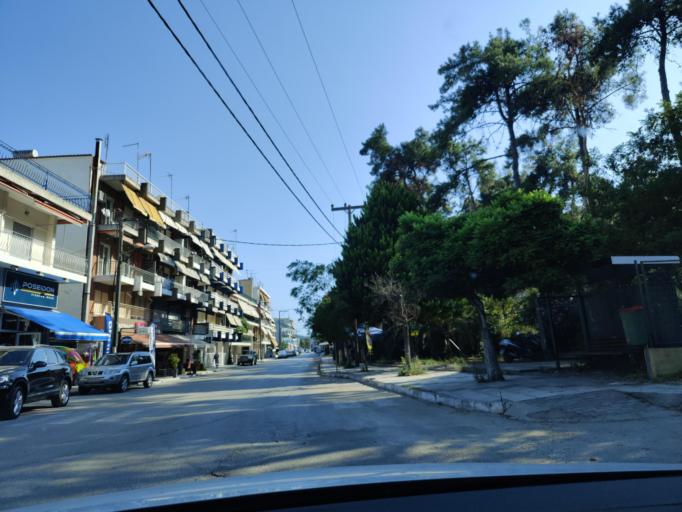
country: GR
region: East Macedonia and Thrace
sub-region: Nomos Kavalas
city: Nea Peramos
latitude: 40.8446
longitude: 24.3062
